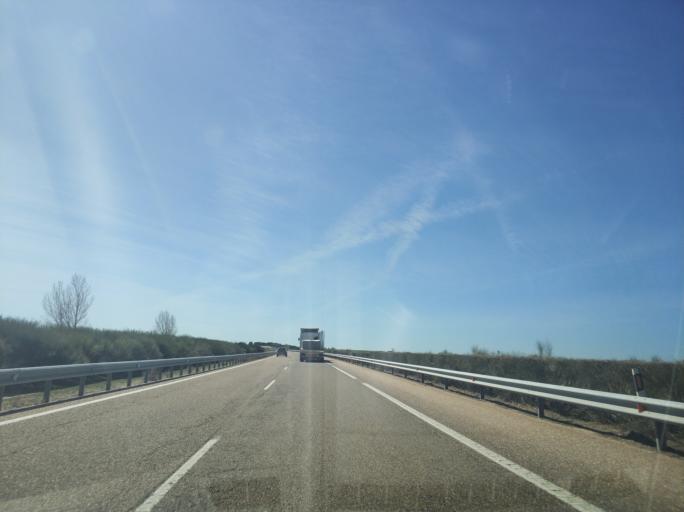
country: ES
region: Castille and Leon
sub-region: Provincia de Valladolid
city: Alaejos
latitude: 41.2793
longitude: -5.2511
